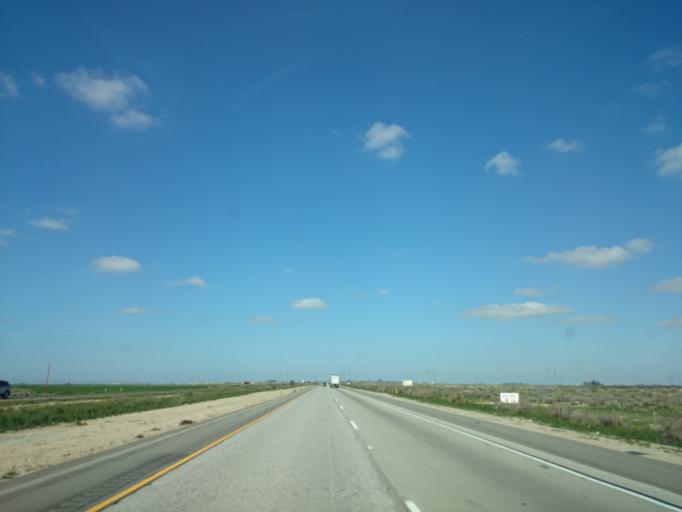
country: US
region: California
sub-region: Kern County
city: Buttonwillow
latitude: 35.3730
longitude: -119.3612
